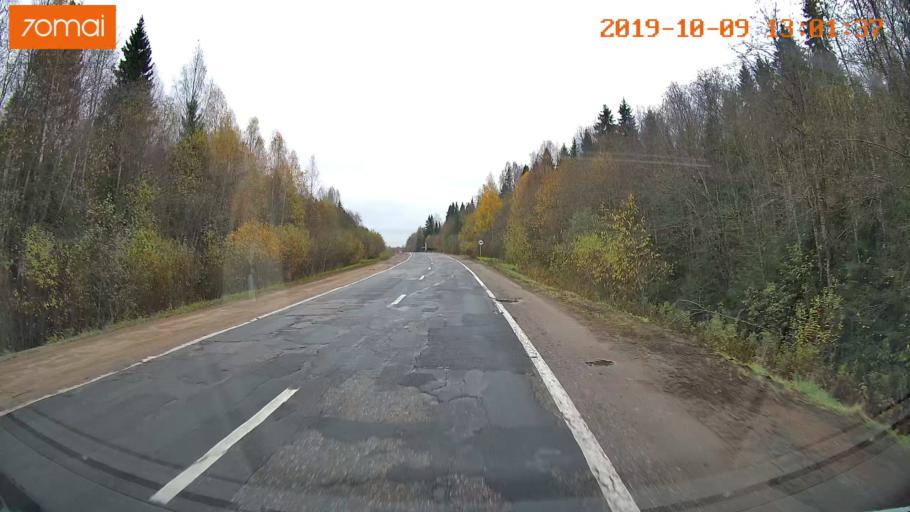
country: RU
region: Jaroslavl
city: Prechistoye
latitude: 58.3669
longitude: 40.4882
